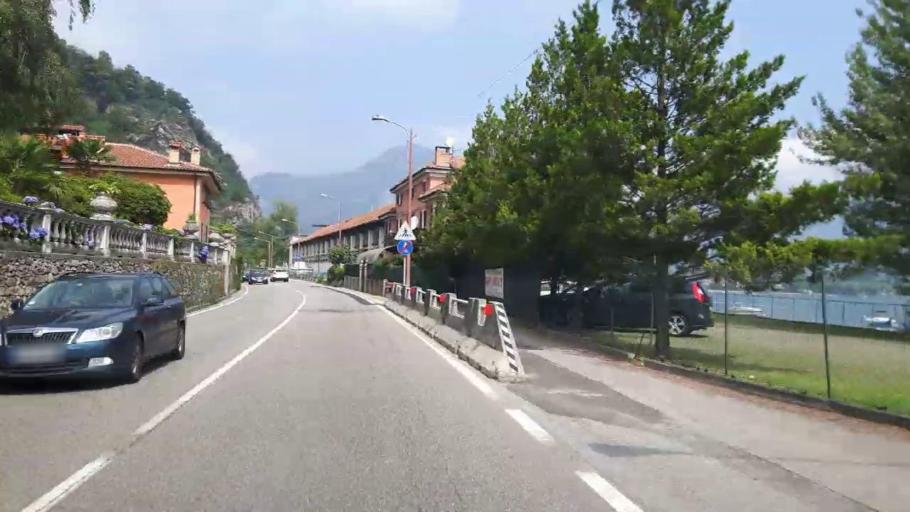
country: IT
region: Piedmont
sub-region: Provincia Verbano-Cusio-Ossola
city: Baveno
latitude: 45.9252
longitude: 8.4872
